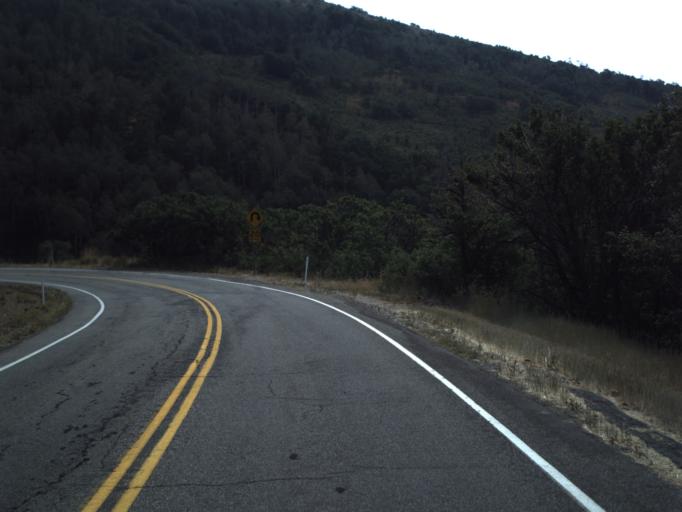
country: US
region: Utah
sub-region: Summit County
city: Summit Park
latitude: 40.8262
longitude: -111.6584
